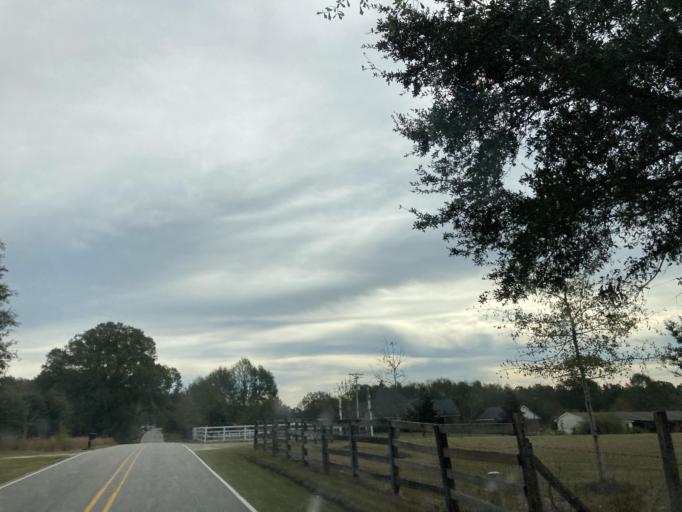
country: US
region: Mississippi
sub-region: Lamar County
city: Purvis
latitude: 31.1127
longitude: -89.4786
